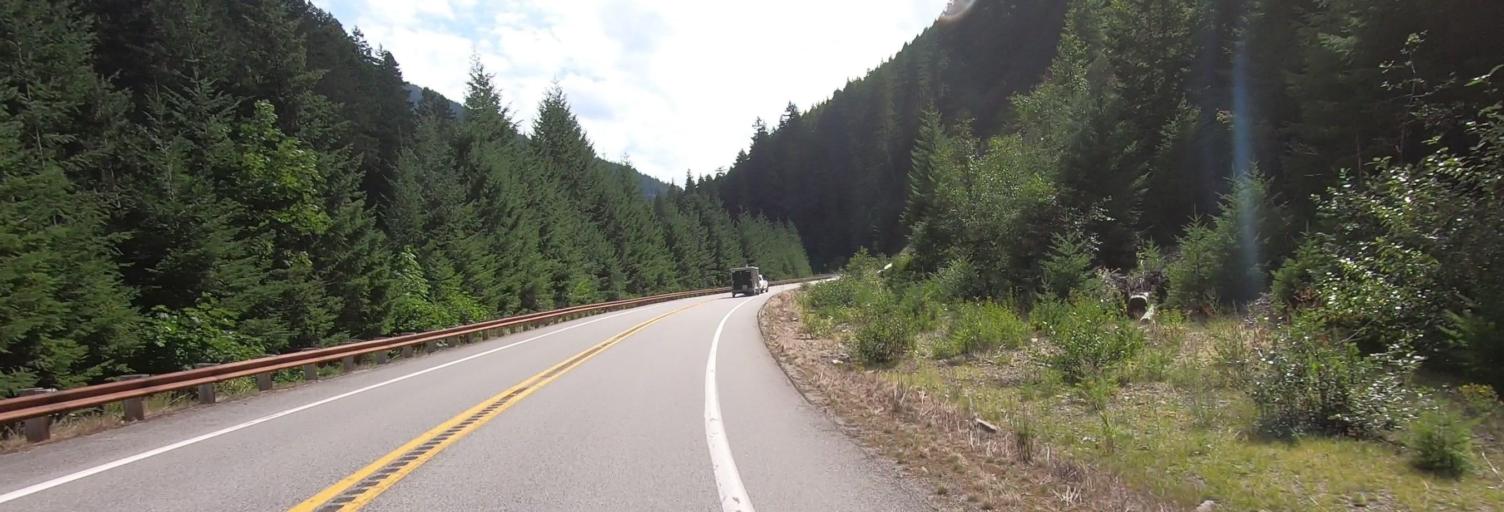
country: US
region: Washington
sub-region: Snohomish County
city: Darrington
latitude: 48.6860
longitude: -120.8987
